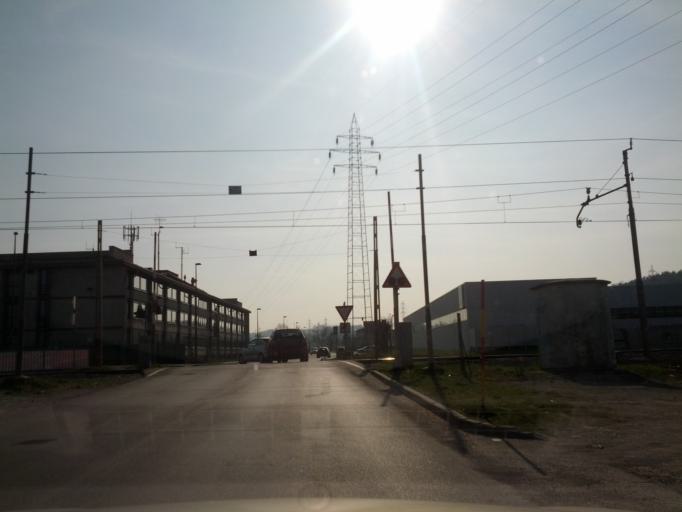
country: SI
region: Ljubljana
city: Ljubljana
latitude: 46.0898
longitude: 14.4774
